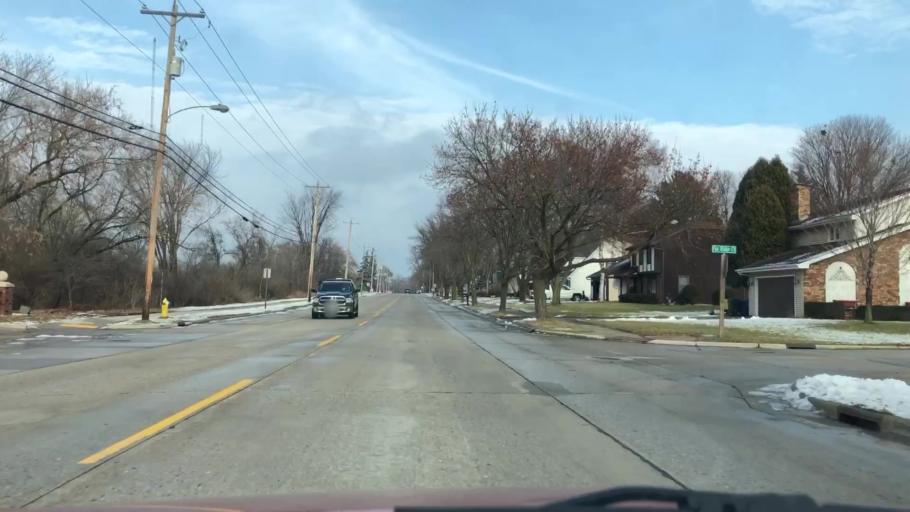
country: US
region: Wisconsin
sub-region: Brown County
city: De Pere
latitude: 44.4326
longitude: -88.0759
